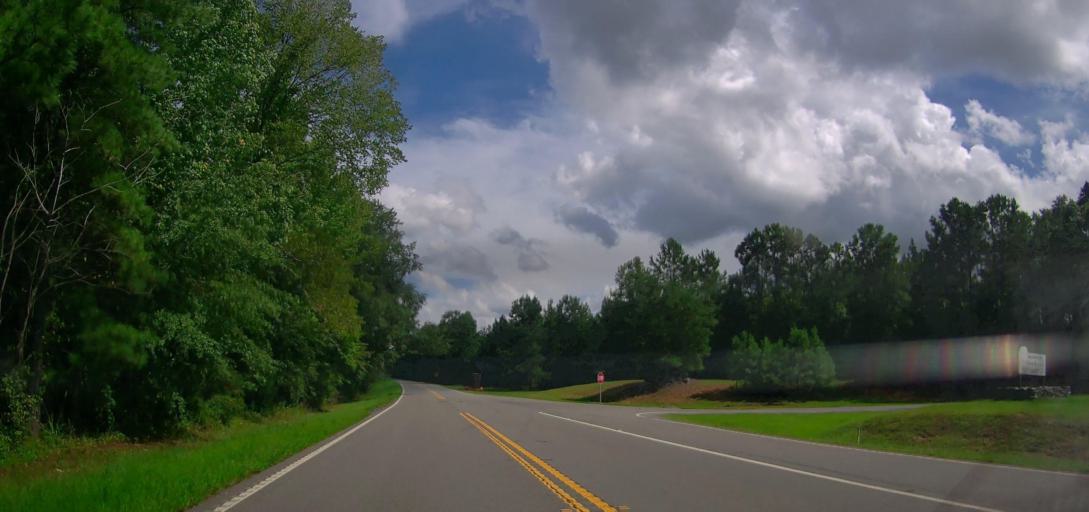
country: US
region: Georgia
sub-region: Talbot County
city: Talbotton
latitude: 32.6430
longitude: -84.5000
